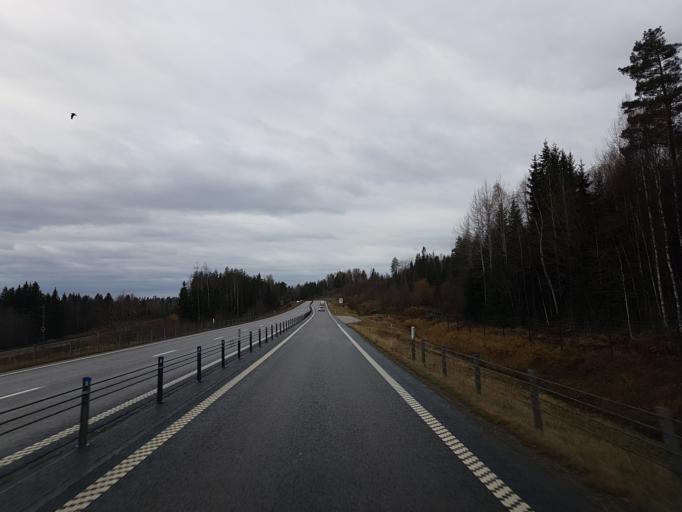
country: SE
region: Vaesternorrland
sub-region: Sundsvalls Kommun
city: Njurundabommen
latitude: 62.0854
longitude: 17.2903
